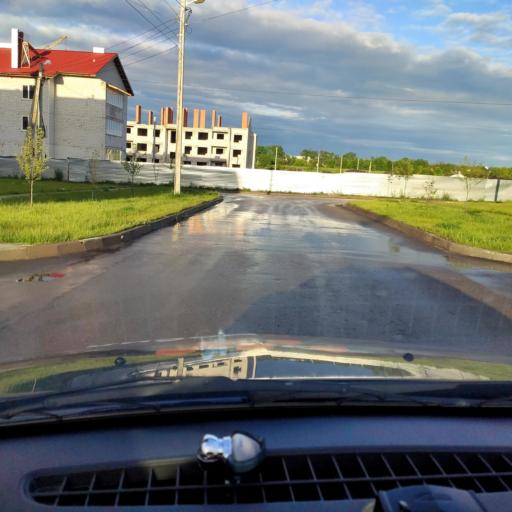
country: RU
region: Voronezj
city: Podgornoye
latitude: 51.7910
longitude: 39.1911
